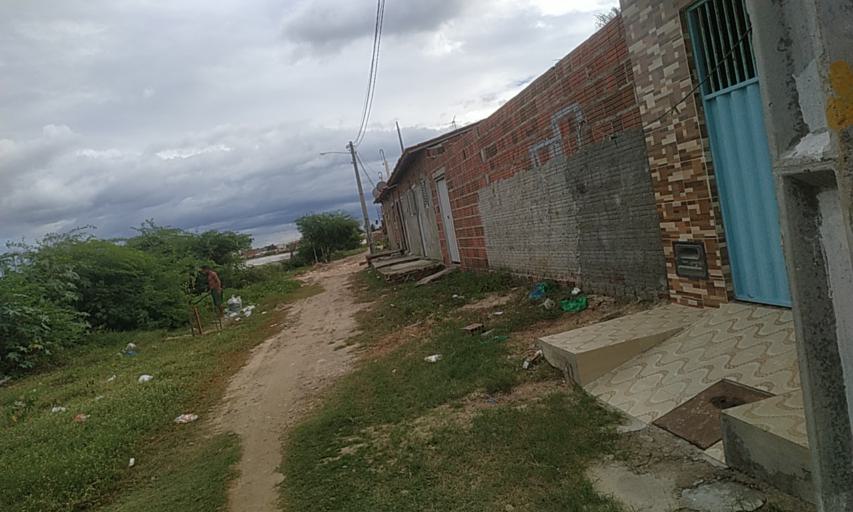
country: BR
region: Rio Grande do Norte
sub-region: Areia Branca
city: Areia Branca
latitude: -4.9560
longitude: -37.1263
